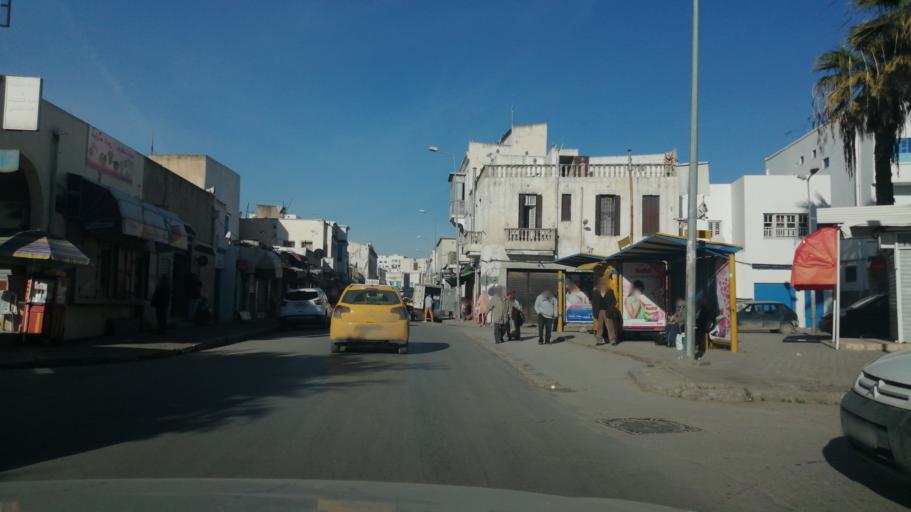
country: TN
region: Tunis
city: Tunis
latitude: 36.8068
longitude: 10.1638
